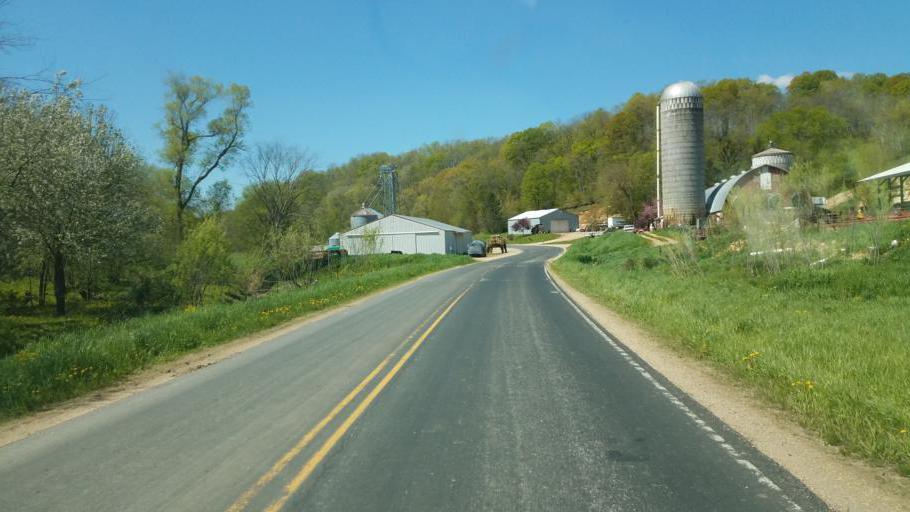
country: US
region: Wisconsin
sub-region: Vernon County
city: Hillsboro
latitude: 43.5754
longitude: -90.3793
